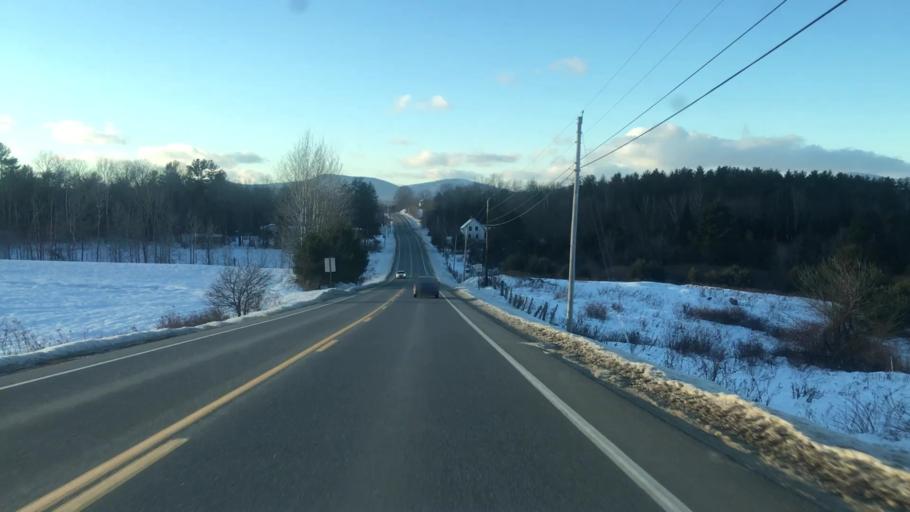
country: US
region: Maine
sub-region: Franklin County
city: Wilton
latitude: 44.5791
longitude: -70.1796
